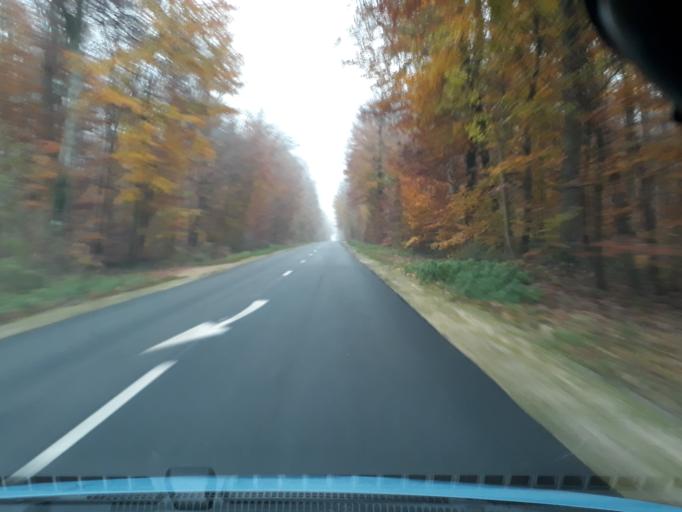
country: FR
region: Ile-de-France
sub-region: Departement de Seine-et-Marne
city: Thomery
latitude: 48.3922
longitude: 2.7714
